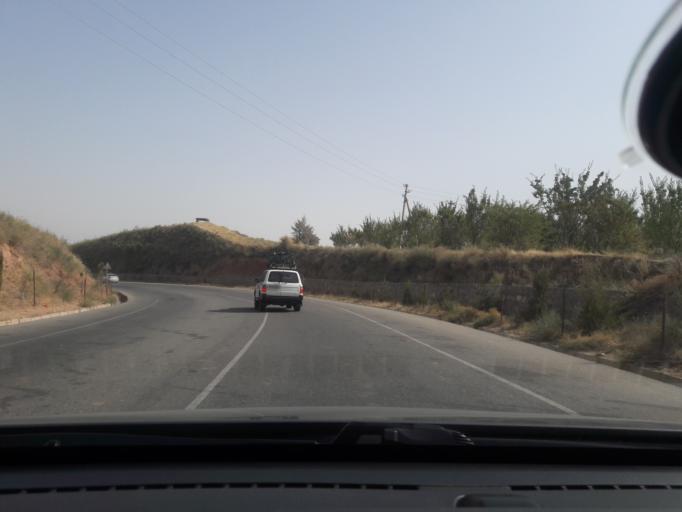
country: TJ
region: Republican Subordination
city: Vahdat
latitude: 38.4880
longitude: 69.1696
